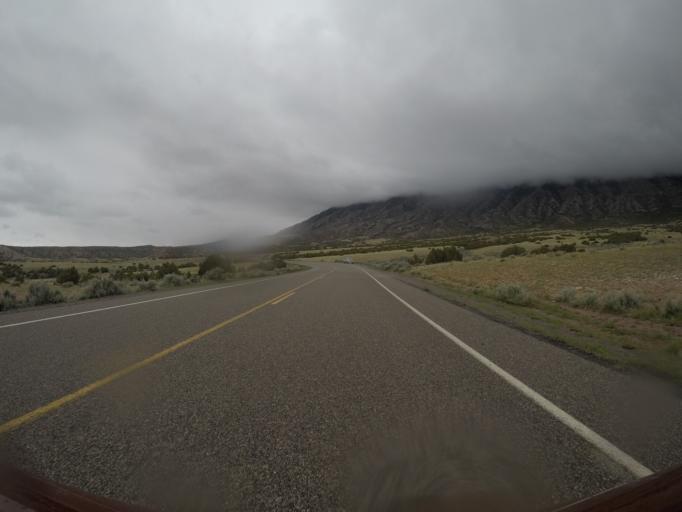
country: US
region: Wyoming
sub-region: Big Horn County
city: Lovell
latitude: 45.0666
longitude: -108.2558
